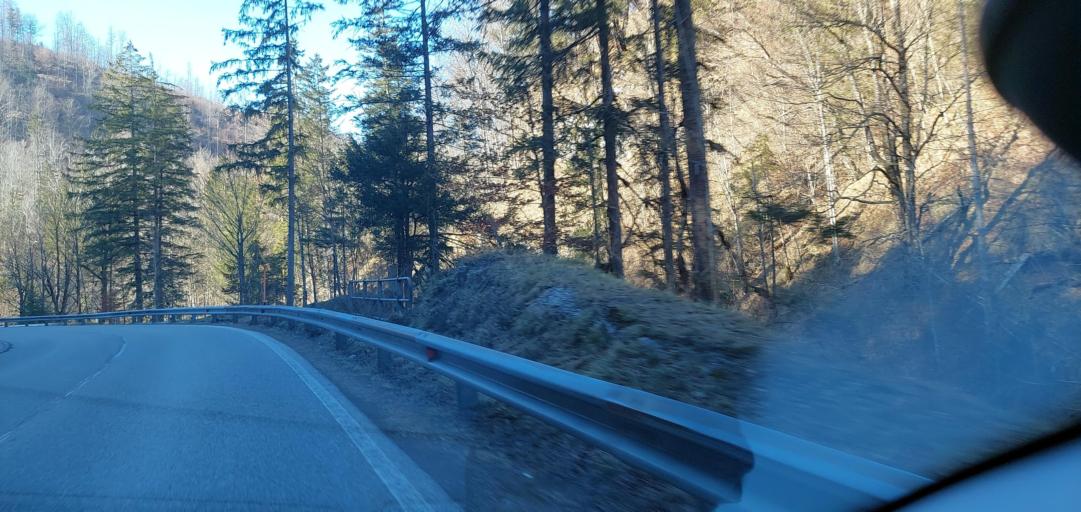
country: AT
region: Upper Austria
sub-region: Politischer Bezirk Gmunden
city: Bad Ischl
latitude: 47.7478
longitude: 13.6617
